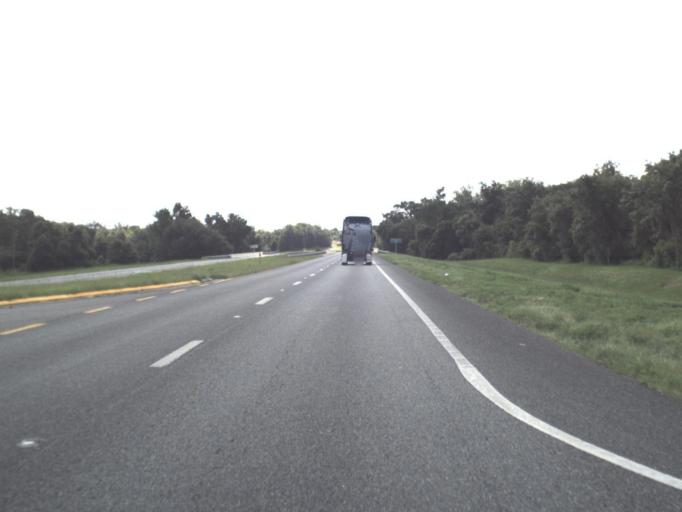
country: US
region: Florida
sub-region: Hernando County
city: Ridge Manor
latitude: 28.5201
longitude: -82.2121
